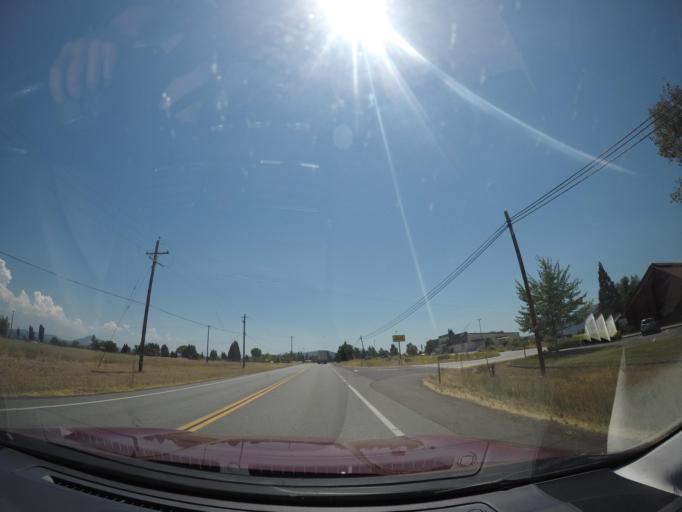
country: US
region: California
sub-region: Shasta County
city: Burney
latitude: 41.0311
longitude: -121.4187
